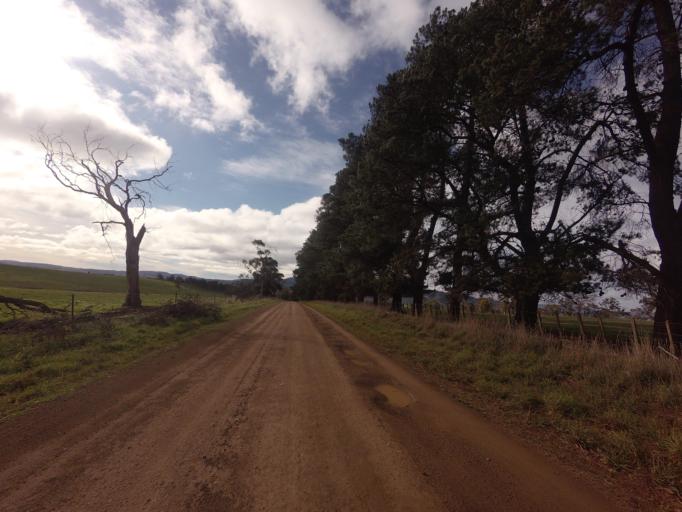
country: AU
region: Tasmania
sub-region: Derwent Valley
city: New Norfolk
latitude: -42.7171
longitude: 146.8793
